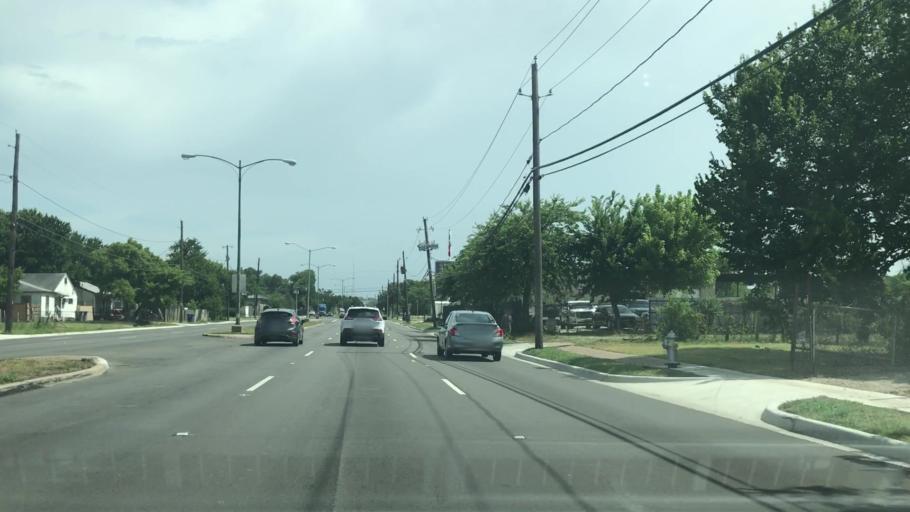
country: US
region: Texas
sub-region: Dallas County
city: Cockrell Hill
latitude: 32.7915
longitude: -96.8738
